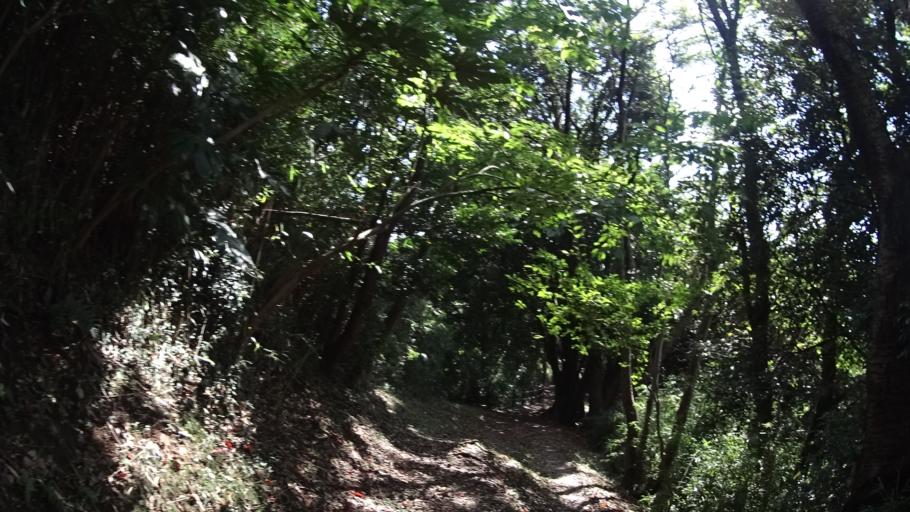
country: JP
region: Kanagawa
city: Kamakura
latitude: 35.3592
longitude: 139.5859
